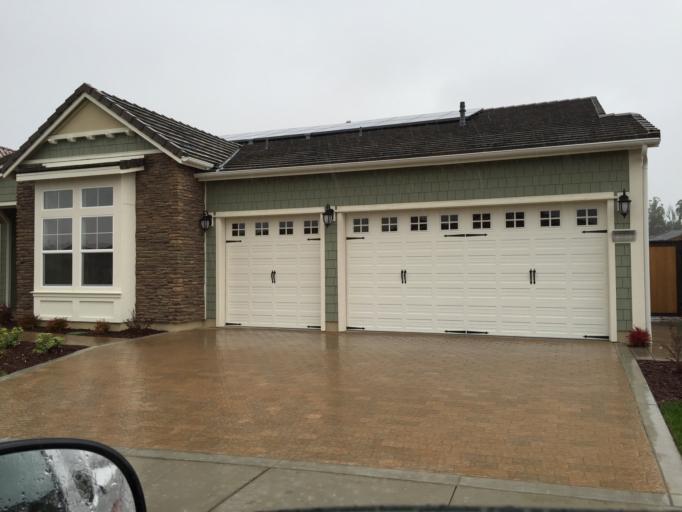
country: US
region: California
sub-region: San Luis Obispo County
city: Callender
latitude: 35.0325
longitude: -120.5449
